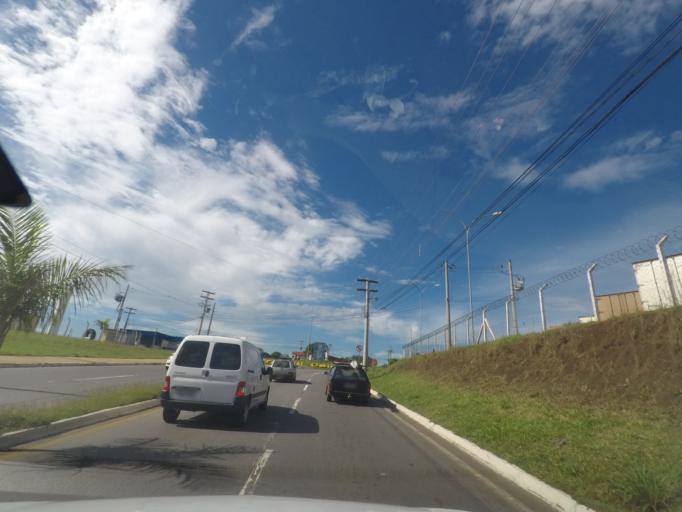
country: BR
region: Goias
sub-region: Aparecida De Goiania
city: Aparecida de Goiania
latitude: -16.7876
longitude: -49.2512
